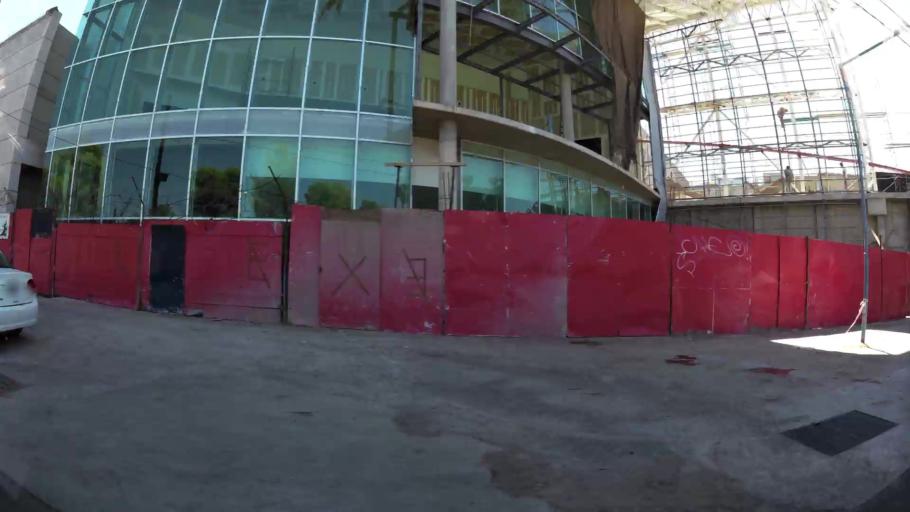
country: AR
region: Mendoza
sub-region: Departamento de Godoy Cruz
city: Godoy Cruz
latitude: -32.9571
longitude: -68.8590
